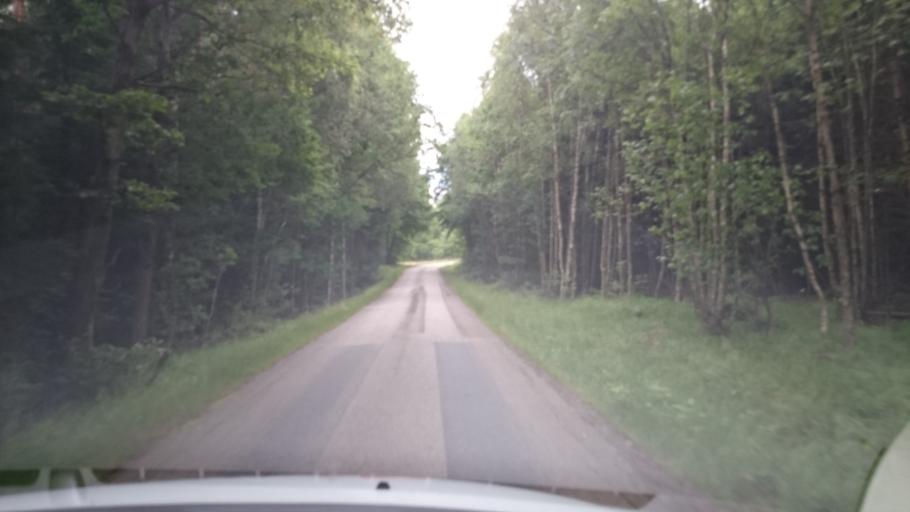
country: SE
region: Halland
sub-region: Hylte Kommun
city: Hyltebruk
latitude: 56.9809
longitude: 13.2123
